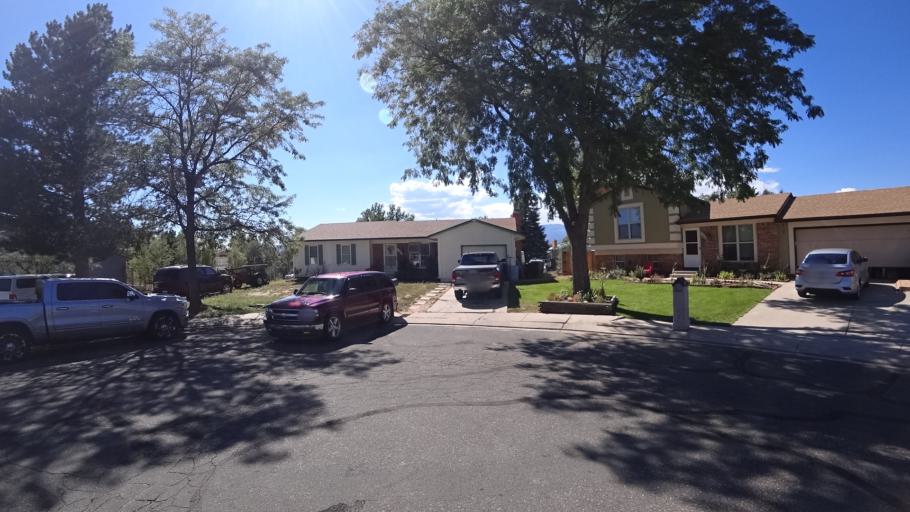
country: US
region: Colorado
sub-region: El Paso County
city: Stratmoor
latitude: 38.7936
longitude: -104.7403
